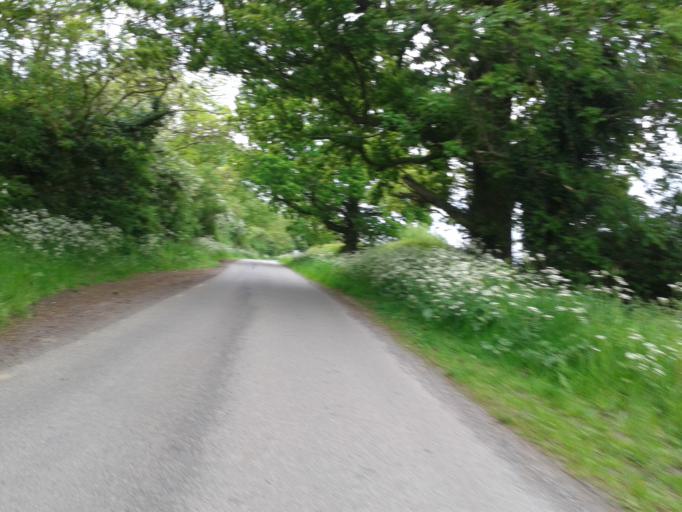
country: GB
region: England
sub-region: Leicestershire
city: Cosby
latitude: 52.5287
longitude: -1.1786
